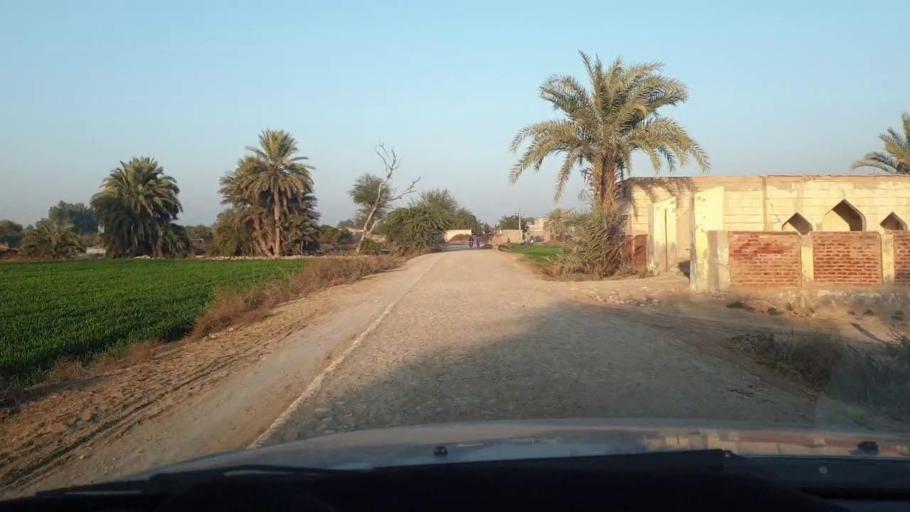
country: PK
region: Sindh
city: Mirpur Mathelo
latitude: 27.9962
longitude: 69.6036
